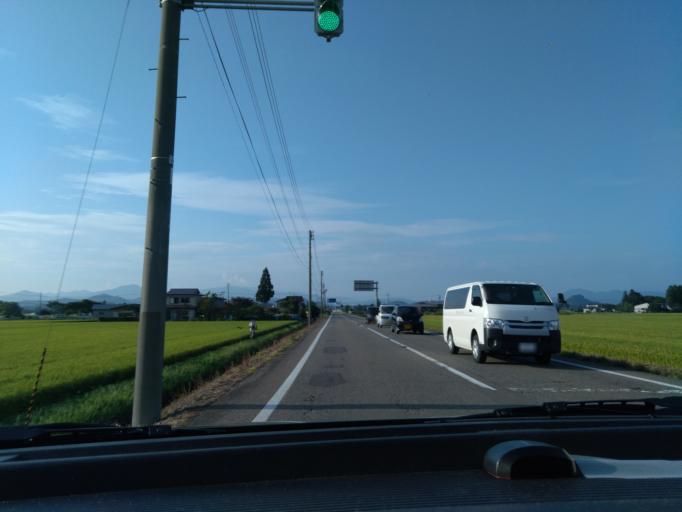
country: JP
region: Akita
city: Kakunodatemachi
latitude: 39.5461
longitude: 140.5578
